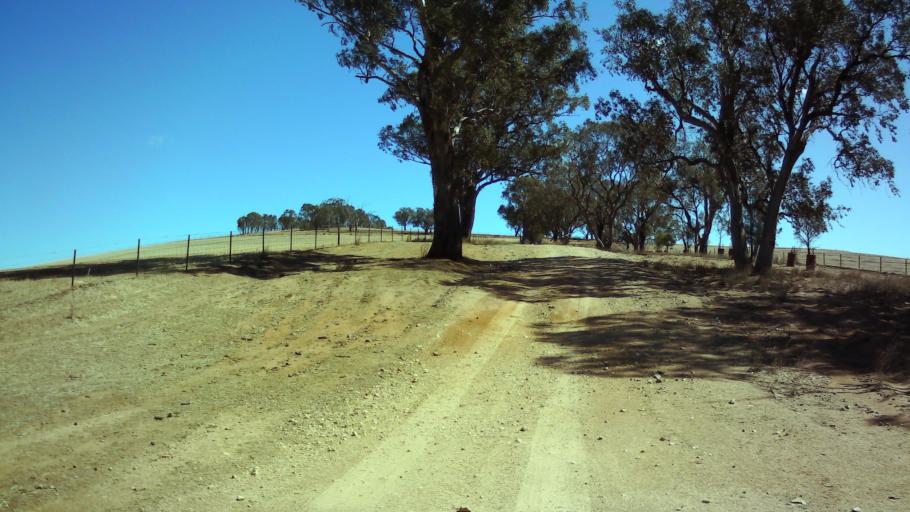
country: AU
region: New South Wales
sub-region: Weddin
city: Grenfell
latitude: -33.9989
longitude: 148.4369
